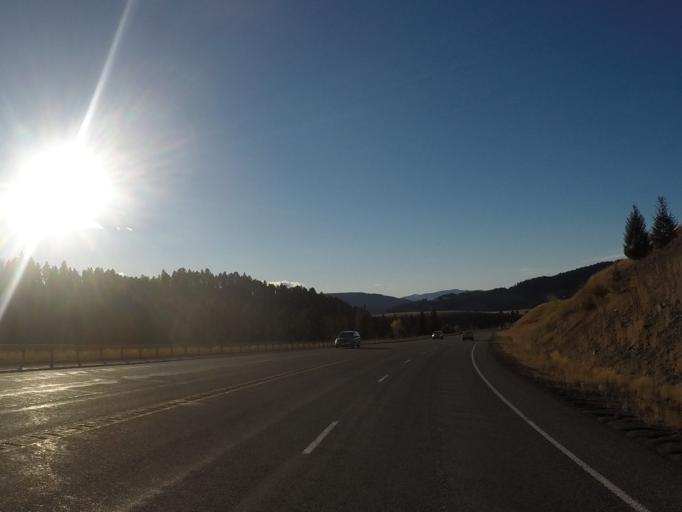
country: US
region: Montana
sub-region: Lewis and Clark County
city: Helena West Side
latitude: 46.5564
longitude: -112.3639
